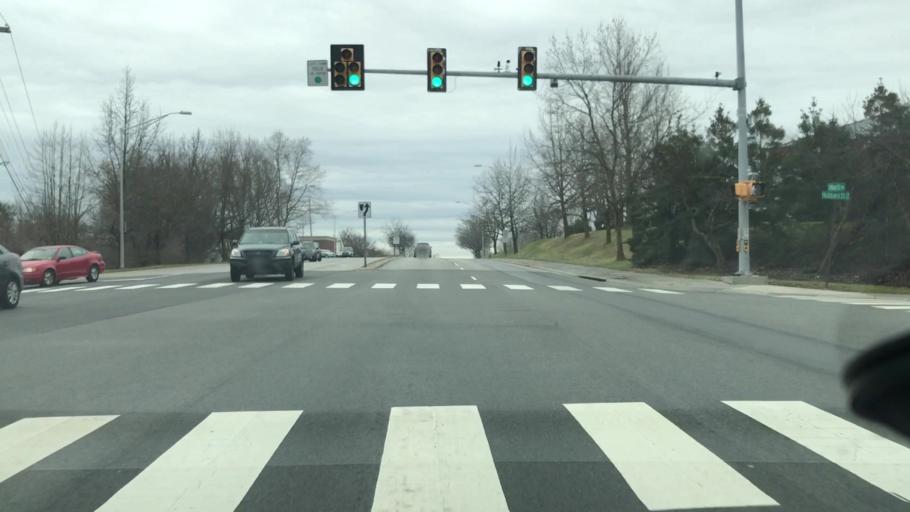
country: US
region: Virginia
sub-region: Montgomery County
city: Blacksburg
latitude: 37.2095
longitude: -80.3994
